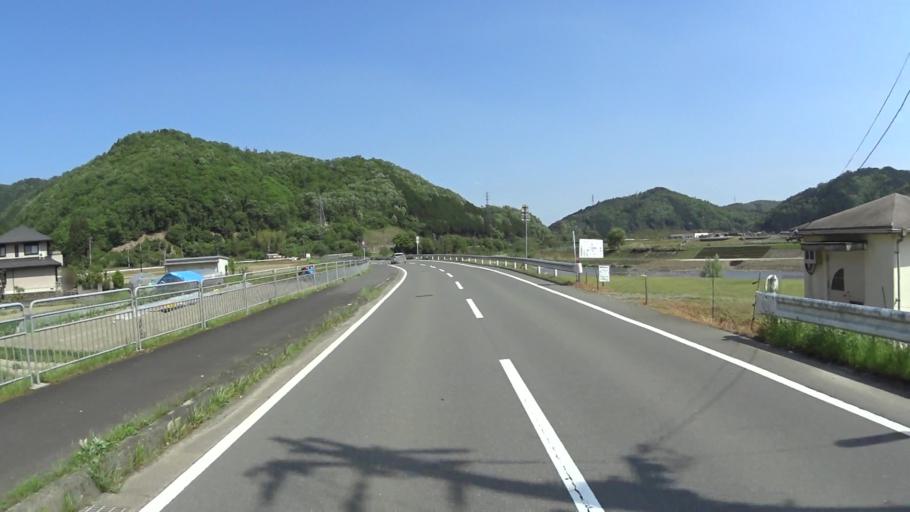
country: JP
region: Kyoto
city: Kameoka
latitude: 35.1261
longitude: 135.5015
